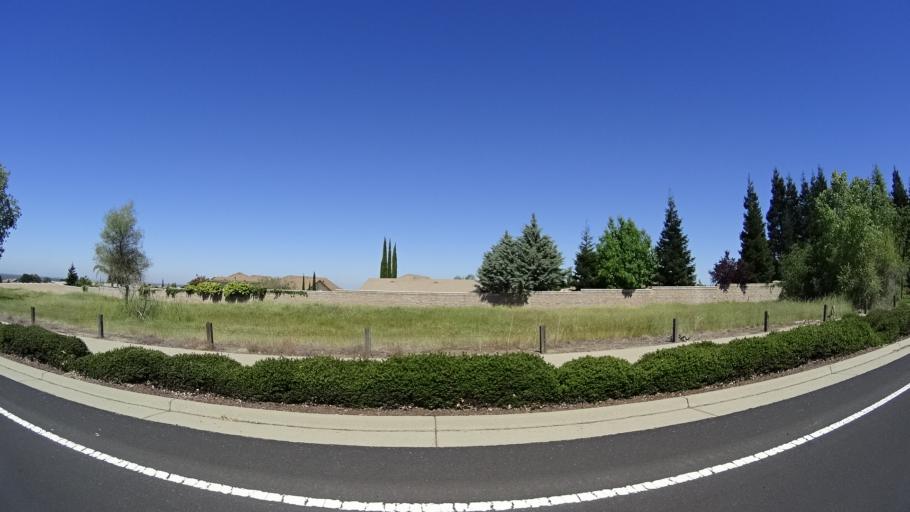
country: US
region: California
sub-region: Placer County
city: Rocklin
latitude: 38.7686
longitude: -121.2212
